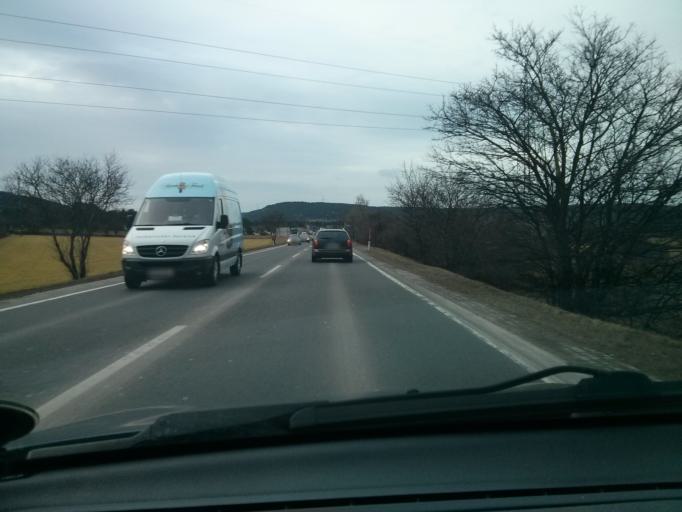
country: AT
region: Lower Austria
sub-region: Politischer Bezirk Wiener Neustadt
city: Theresienfeld
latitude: 47.8539
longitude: 16.1900
